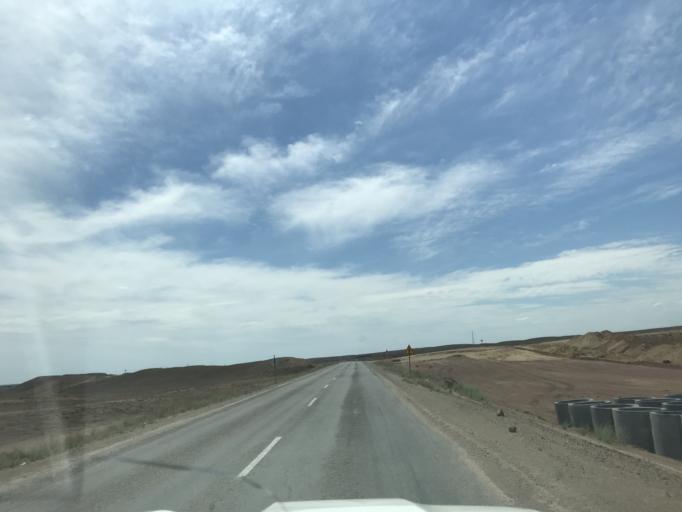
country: KZ
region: Almaty Oblysy
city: Ulken
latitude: 45.0806
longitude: 73.9723
